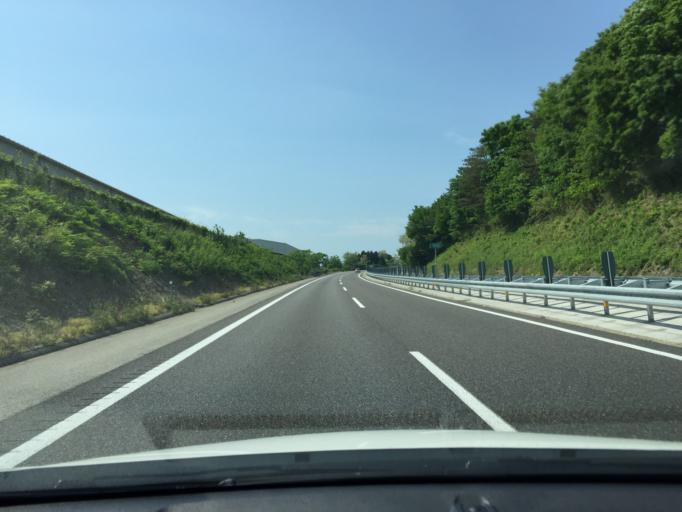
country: JP
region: Fukushima
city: Sukagawa
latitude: 37.2096
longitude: 140.3082
